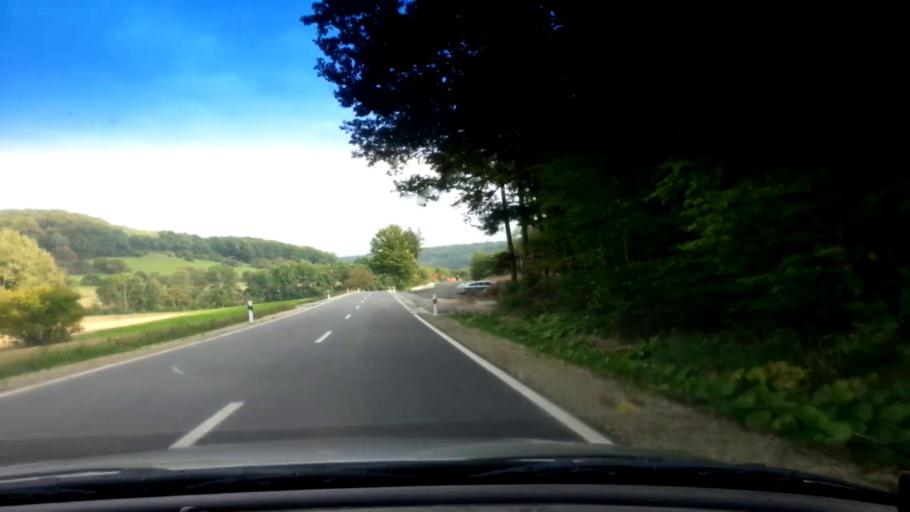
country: DE
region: Bavaria
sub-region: Upper Franconia
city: Schesslitz
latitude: 50.0011
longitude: 11.0661
